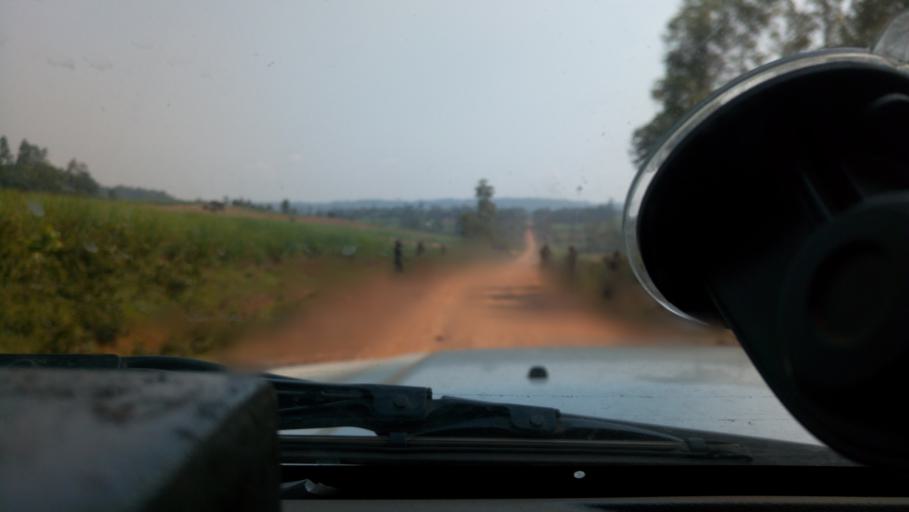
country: KE
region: Kisii
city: Ogembo
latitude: -0.8670
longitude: 34.6131
